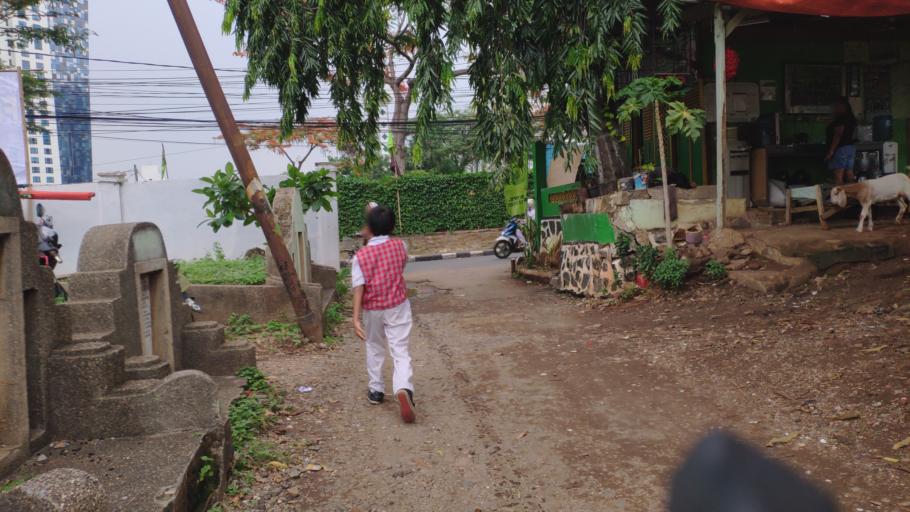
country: ID
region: Jakarta Raya
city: Jakarta
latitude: -6.2213
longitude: 106.8406
